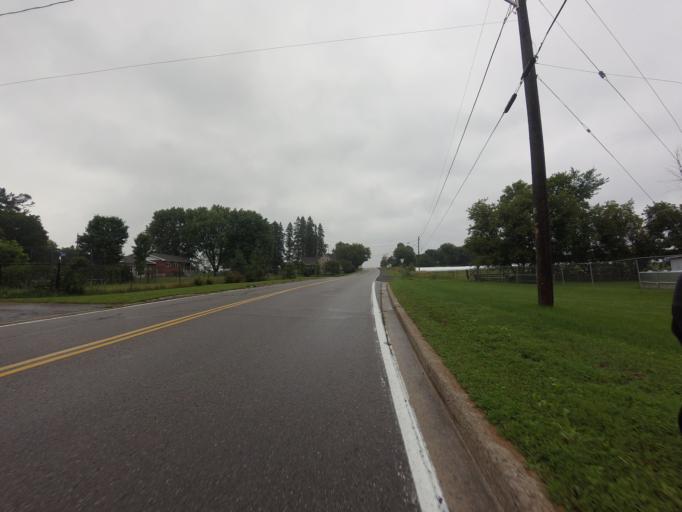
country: CA
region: Ontario
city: Perth
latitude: 45.0812
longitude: -76.4429
